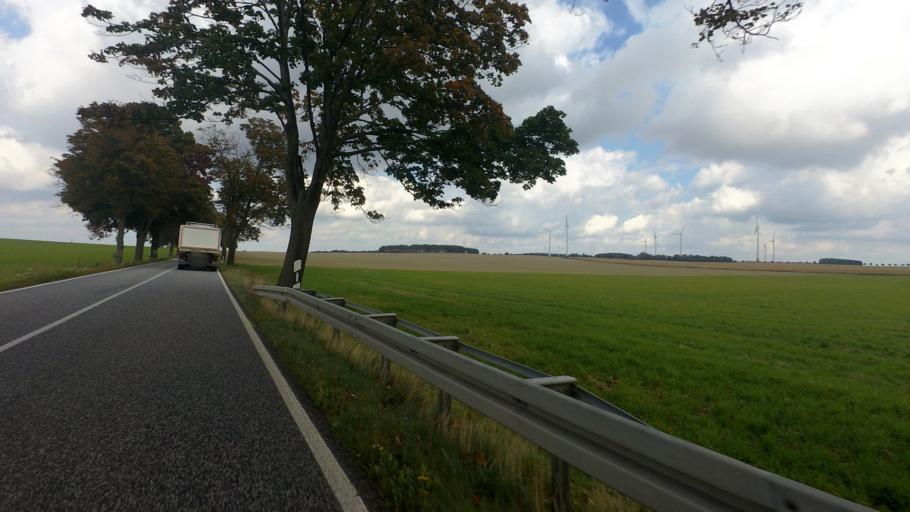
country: DE
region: Brandenburg
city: Juterbog
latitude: 51.9564
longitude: 13.1130
